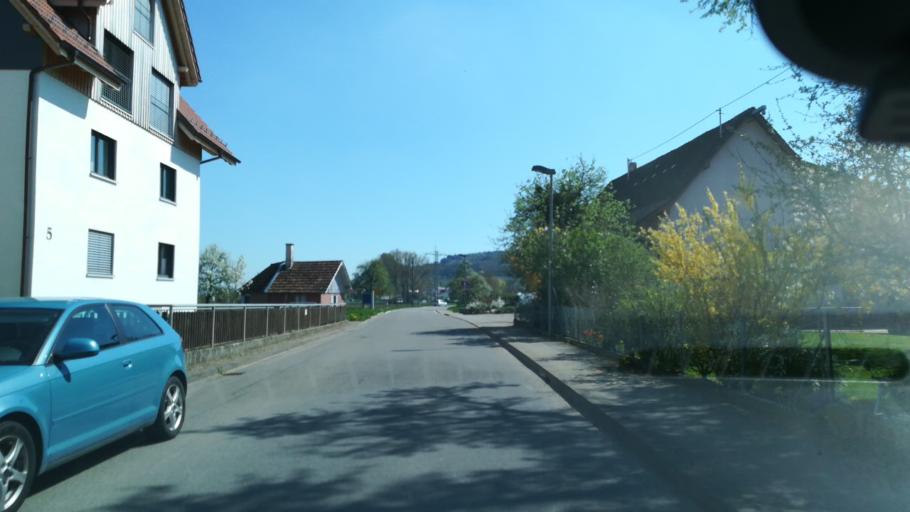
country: DE
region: Baden-Wuerttemberg
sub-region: Freiburg Region
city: Muhlhausen-Ehingen
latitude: 47.8225
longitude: 8.8002
